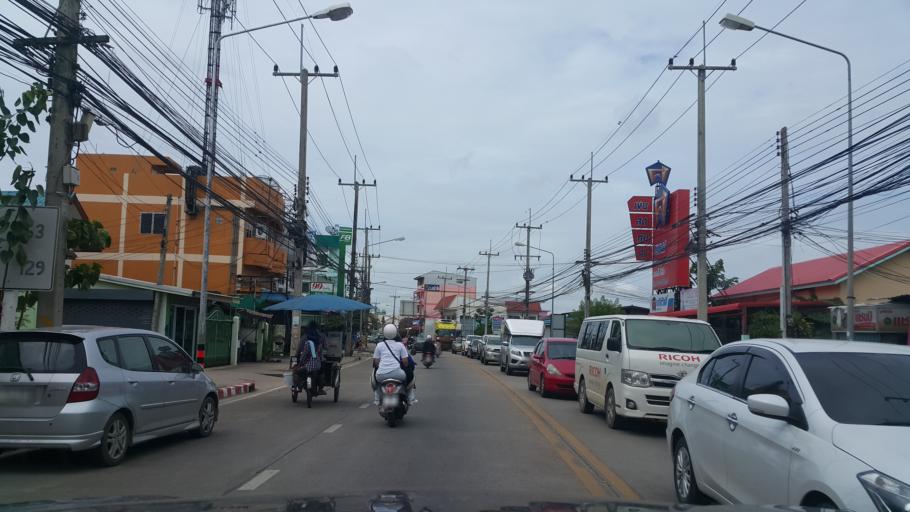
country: TH
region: Phitsanulok
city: Phitsanulok
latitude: 16.8292
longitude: 100.2474
